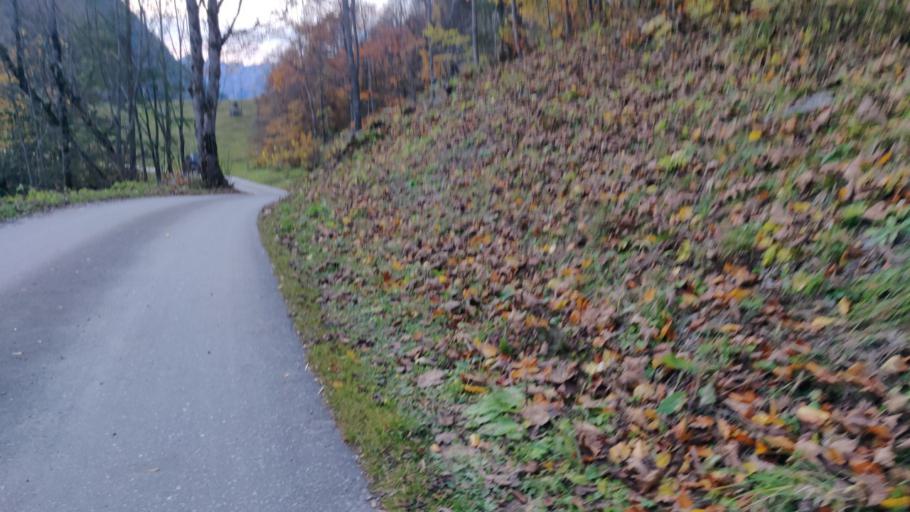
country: CH
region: Obwalden
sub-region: Obwalden
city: Engelberg
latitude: 46.7952
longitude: 8.4661
